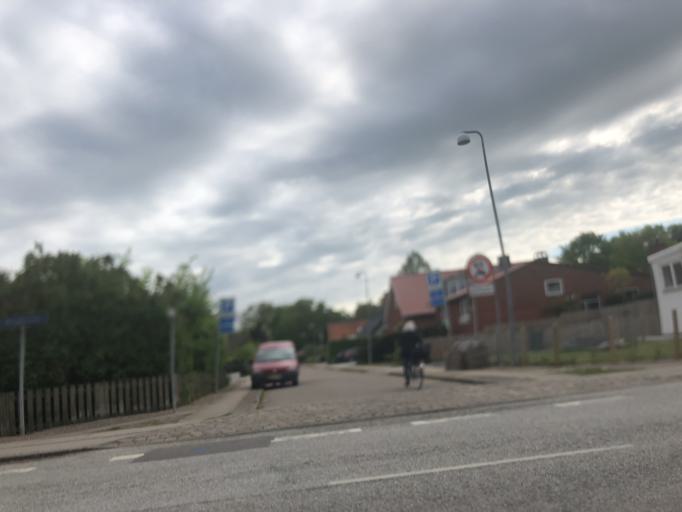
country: DK
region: Zealand
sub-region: Koge Kommune
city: Koge
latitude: 55.4552
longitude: 12.1774
